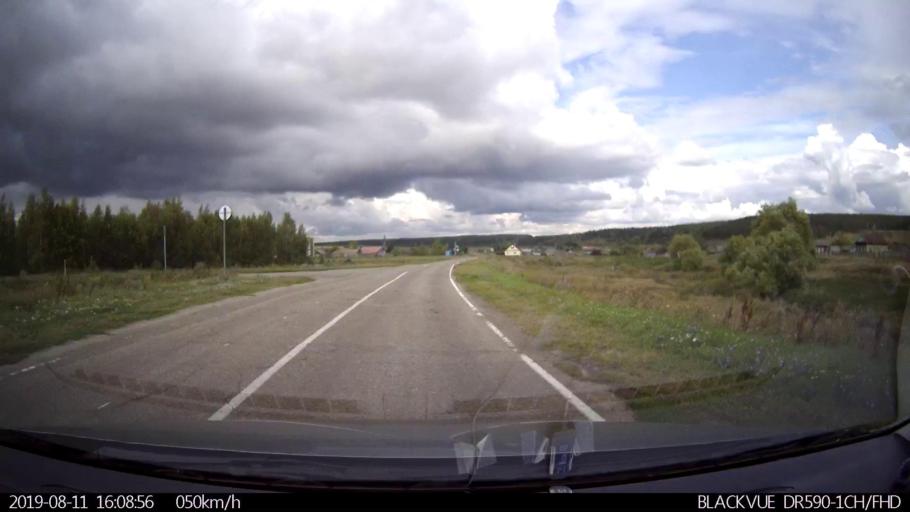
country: RU
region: Ulyanovsk
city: Ignatovka
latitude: 53.9886
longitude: 47.6502
